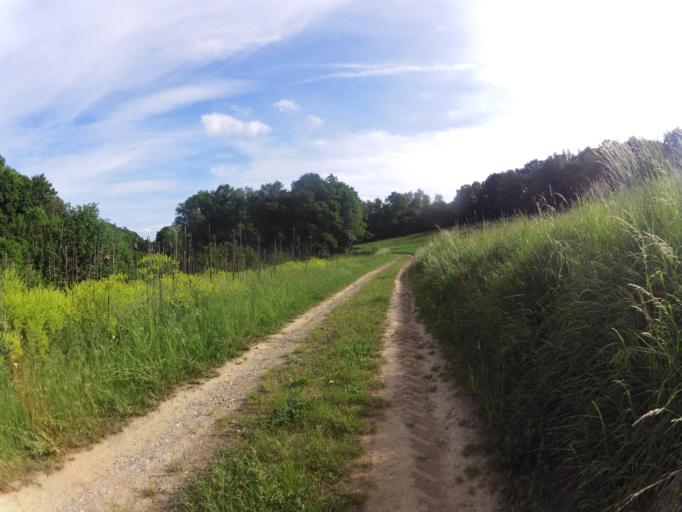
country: DE
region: Bavaria
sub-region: Regierungsbezirk Unterfranken
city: Frickenhausen
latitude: 49.6810
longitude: 10.0767
